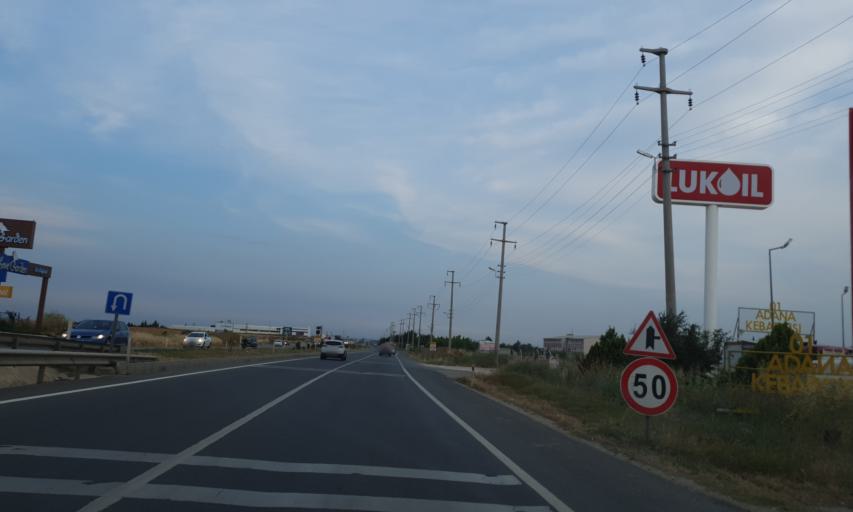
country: TR
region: Kirklareli
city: Luleburgaz
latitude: 41.3847
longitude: 27.3925
